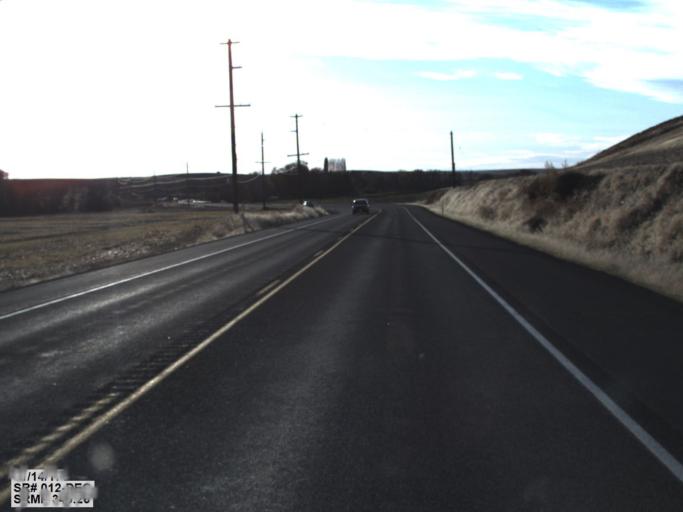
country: US
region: Washington
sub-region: Walla Walla County
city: Walla Walla East
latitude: 46.1241
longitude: -118.2034
